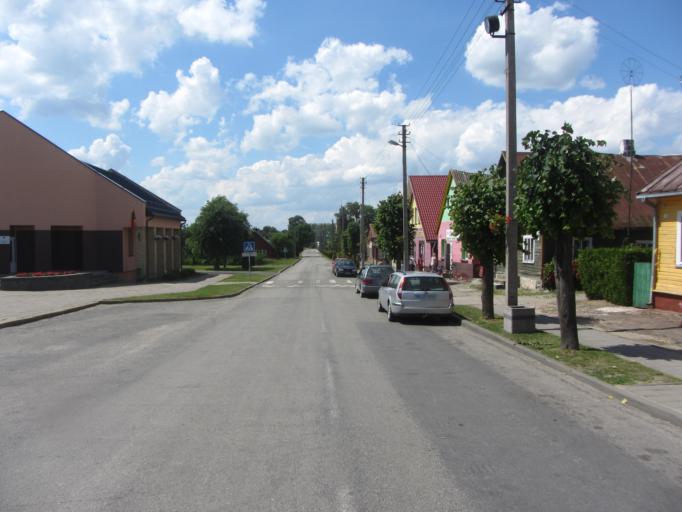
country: LT
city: Jieznas
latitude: 54.5013
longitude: 24.2520
